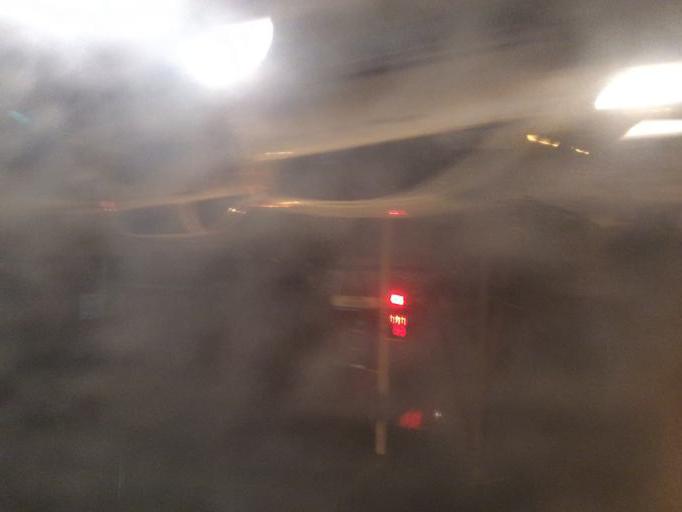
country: KZ
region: Astana Qalasy
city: Astana
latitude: 51.1644
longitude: 71.4582
